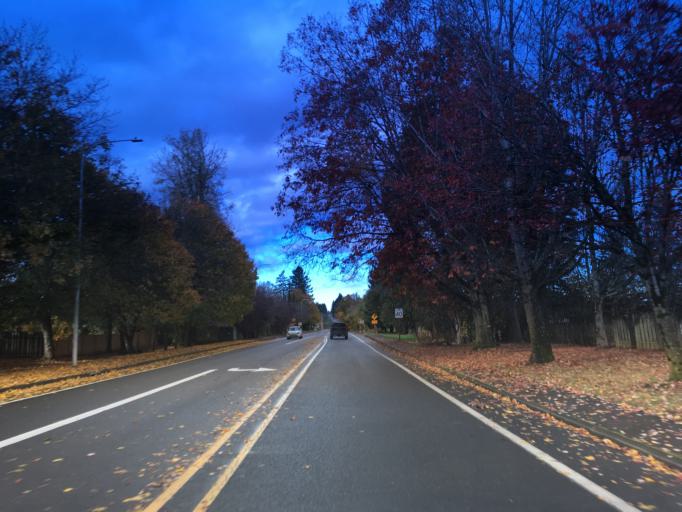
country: US
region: Oregon
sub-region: Multnomah County
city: Troutdale
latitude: 45.5190
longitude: -122.3784
